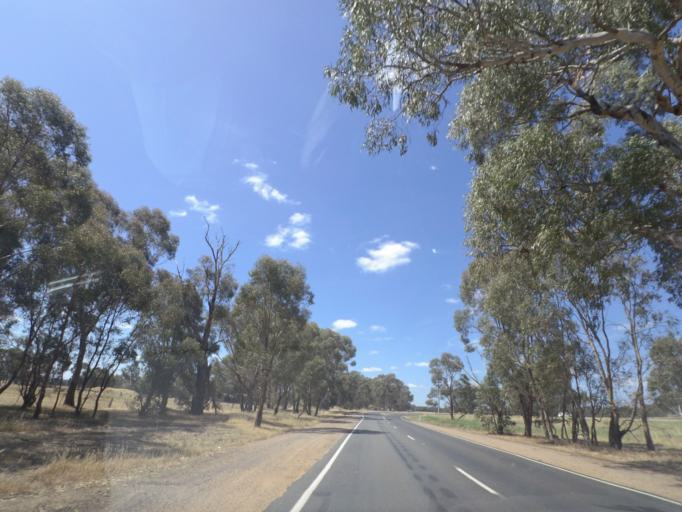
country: AU
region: Victoria
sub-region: Wangaratta
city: Wangaratta
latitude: -36.4079
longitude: 146.2713
